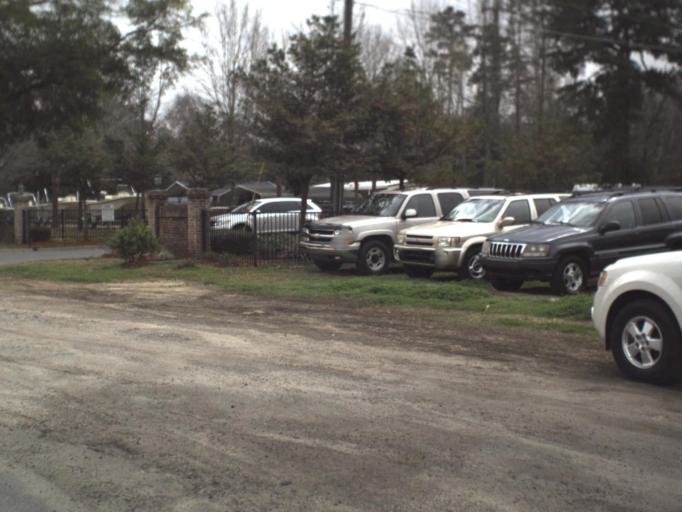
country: US
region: Florida
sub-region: Leon County
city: Tallahassee
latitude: 30.4291
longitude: -84.1988
